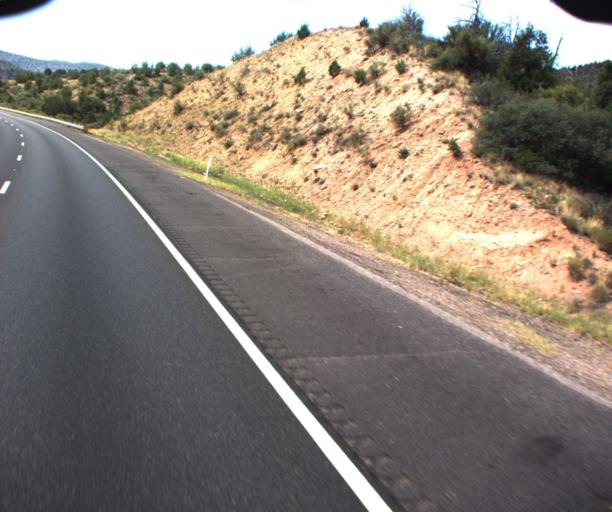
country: US
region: Arizona
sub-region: Yavapai County
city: Camp Verde
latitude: 34.5482
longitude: -111.9098
